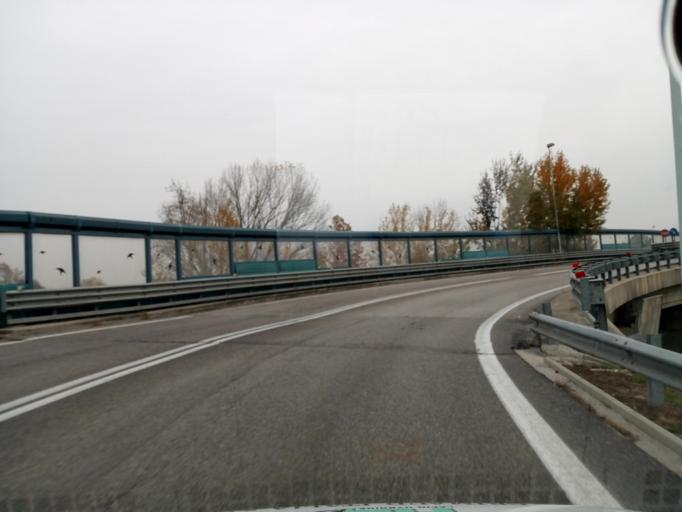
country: IT
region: Veneto
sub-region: Provincia di Padova
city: Cadoneghe
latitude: 45.4285
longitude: 11.9236
